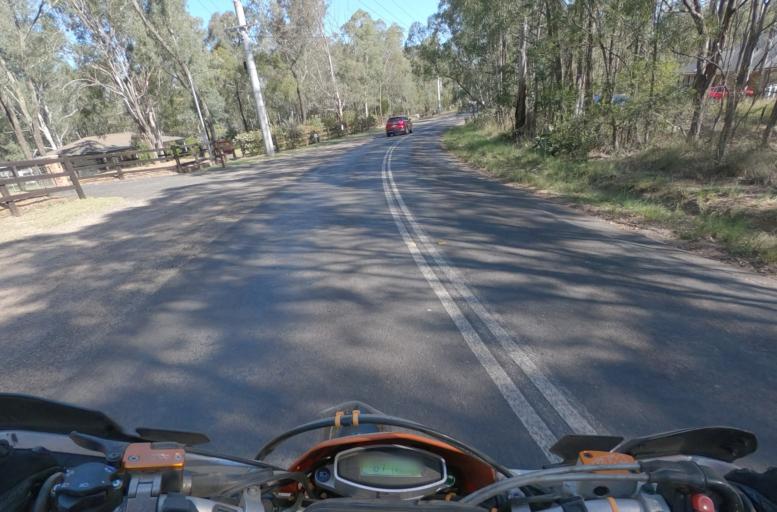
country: AU
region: New South Wales
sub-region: Hawkesbury
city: Scheyville
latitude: -33.5757
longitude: 150.9073
